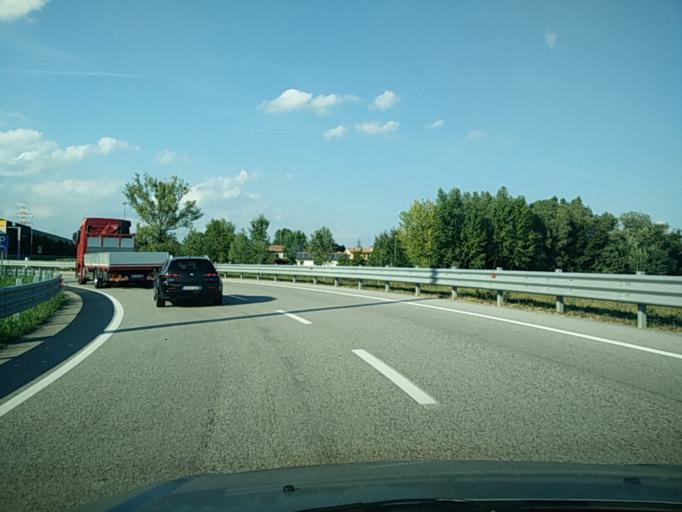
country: IT
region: Veneto
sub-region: Provincia di Venezia
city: Marano
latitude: 45.4801
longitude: 12.1322
